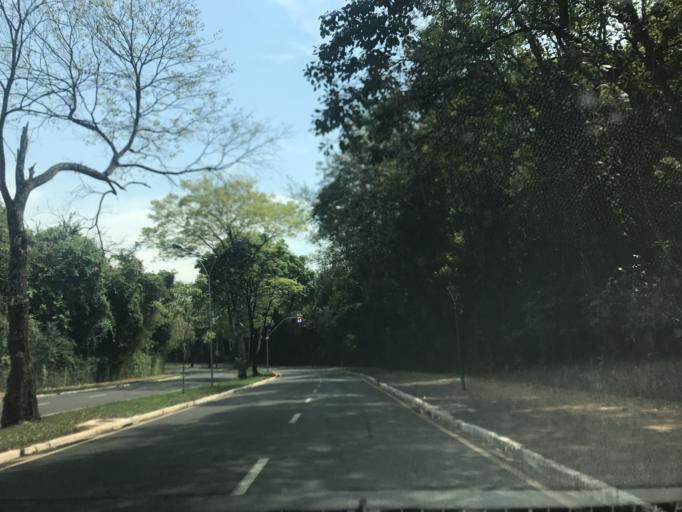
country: BR
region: Parana
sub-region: Maringa
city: Maringa
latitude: -23.4364
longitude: -51.9409
